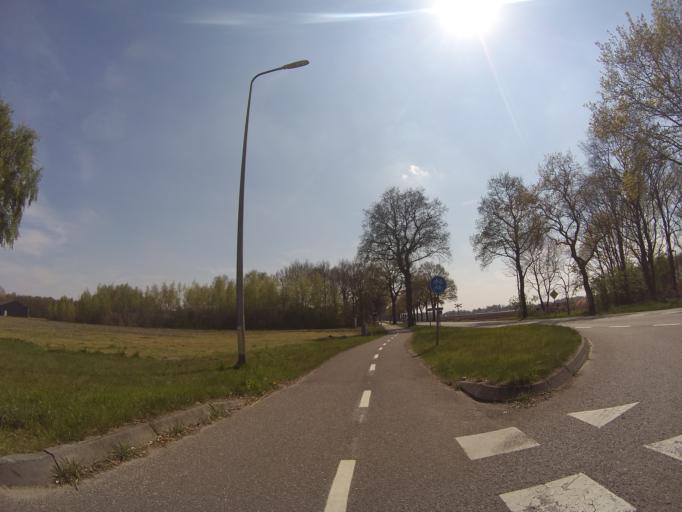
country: NL
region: Drenthe
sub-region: Gemeente Emmen
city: Schoonebeek
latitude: 52.6824
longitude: 6.8712
